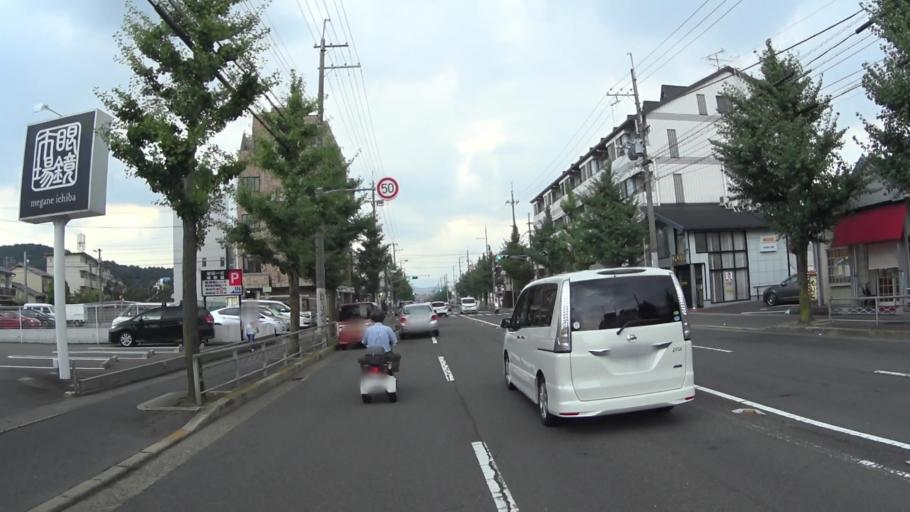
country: JP
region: Kyoto
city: Kyoto
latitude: 35.0203
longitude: 135.7073
